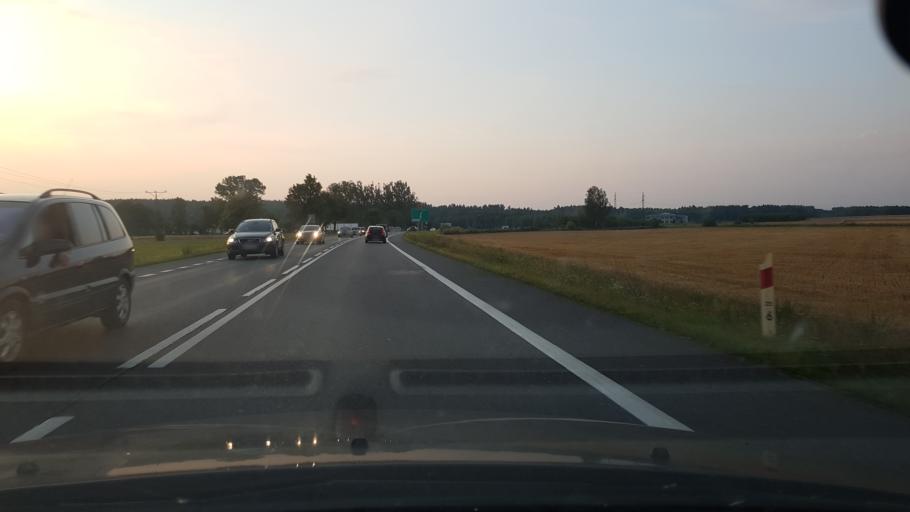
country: PL
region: Masovian Voivodeship
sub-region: Powiat mlawski
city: Mlawa
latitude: 53.1237
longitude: 20.3942
